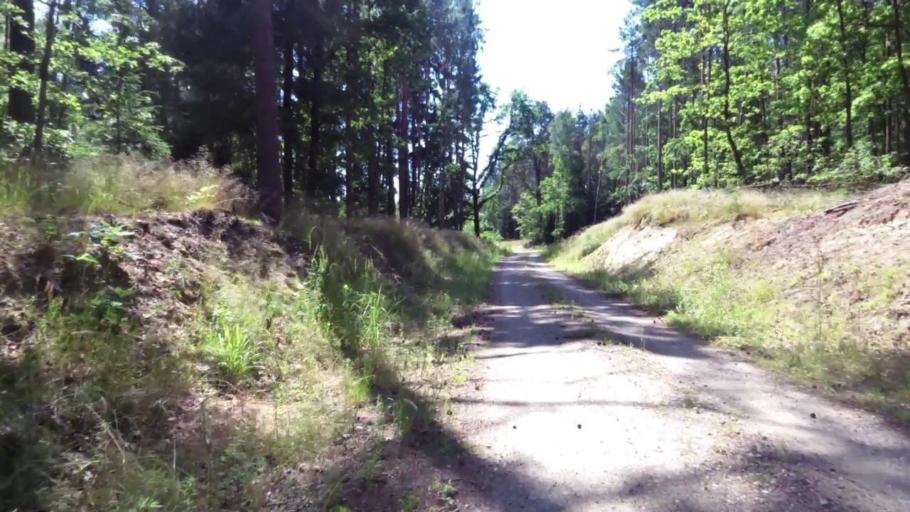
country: PL
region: West Pomeranian Voivodeship
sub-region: Powiat swidwinski
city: Polczyn-Zdroj
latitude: 53.7969
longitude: 16.1146
